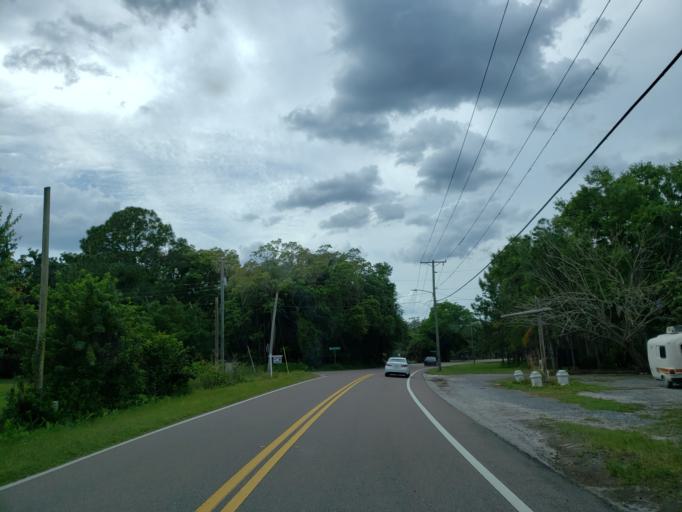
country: US
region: Florida
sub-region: Hillsborough County
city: Keystone
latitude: 28.1326
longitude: -82.6279
